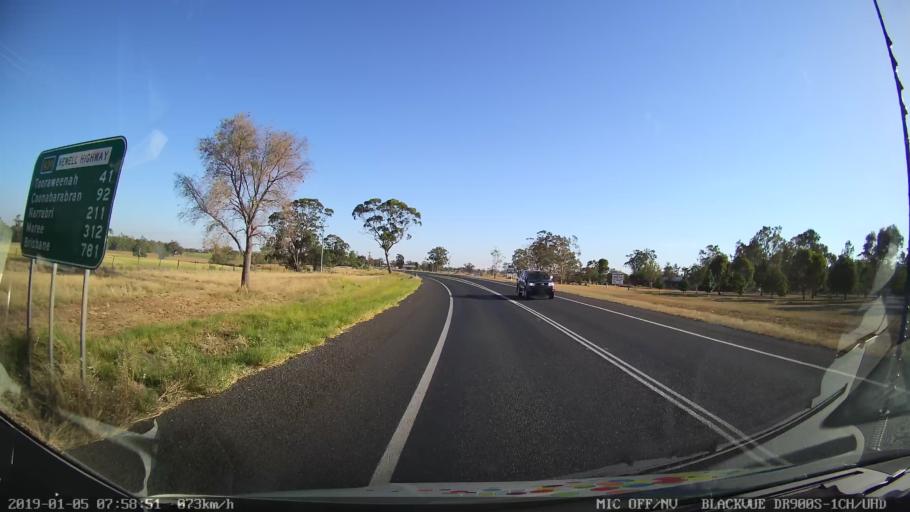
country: AU
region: New South Wales
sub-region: Gilgandra
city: Gilgandra
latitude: -31.7088
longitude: 148.6790
